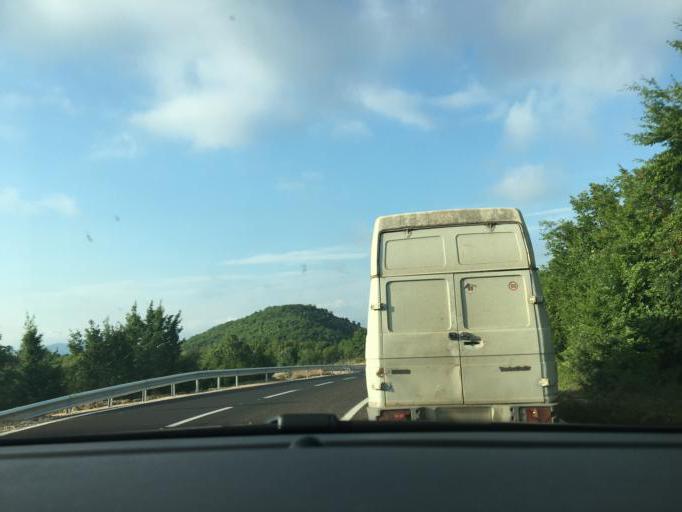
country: MK
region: Valandovo
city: Valandovo
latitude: 41.3393
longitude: 22.5882
